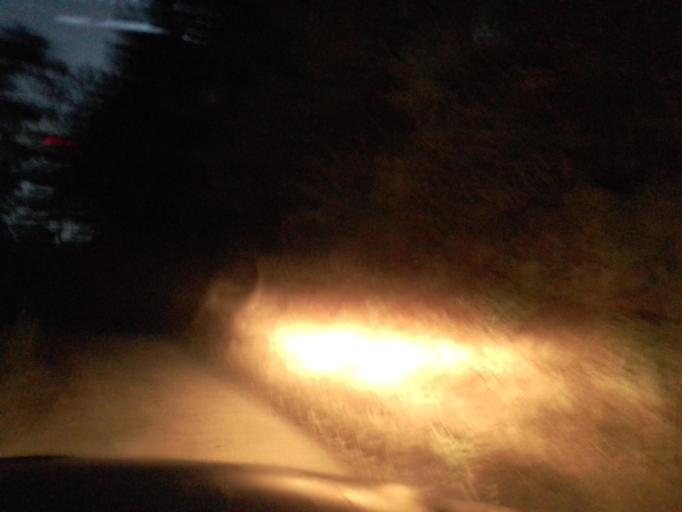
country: GT
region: San Marcos
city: Tacana
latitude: 15.2366
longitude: -92.1981
